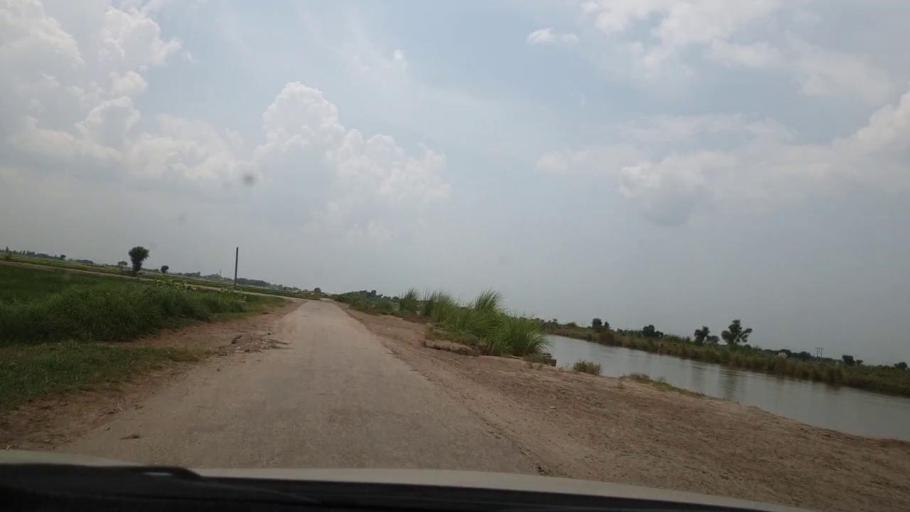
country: PK
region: Sindh
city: Goth Garelo
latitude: 27.4287
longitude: 68.1066
